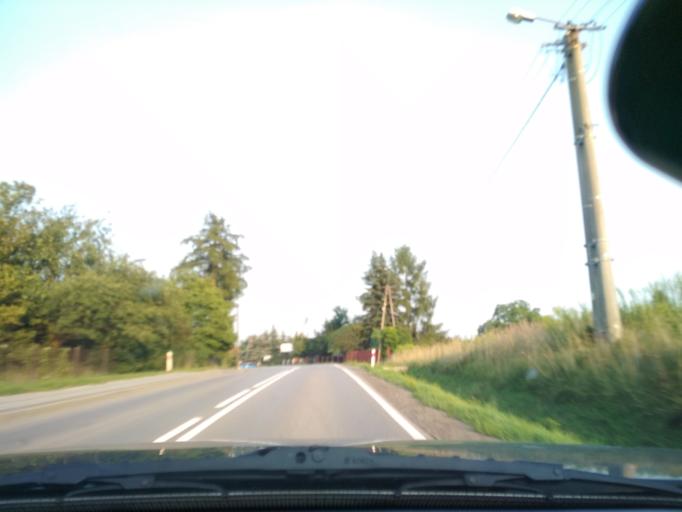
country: PL
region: Lesser Poland Voivodeship
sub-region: Powiat olkuski
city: Wolbrom
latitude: 50.3928
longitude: 19.7458
